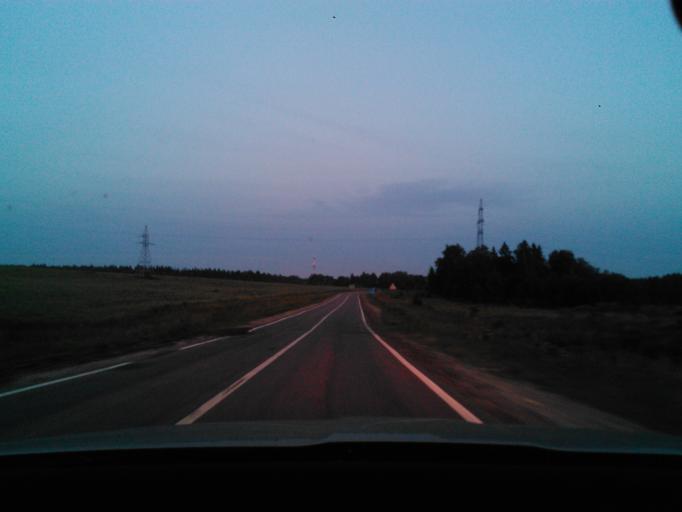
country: RU
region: Moskovskaya
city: Klin
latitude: 56.1535
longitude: 36.7676
